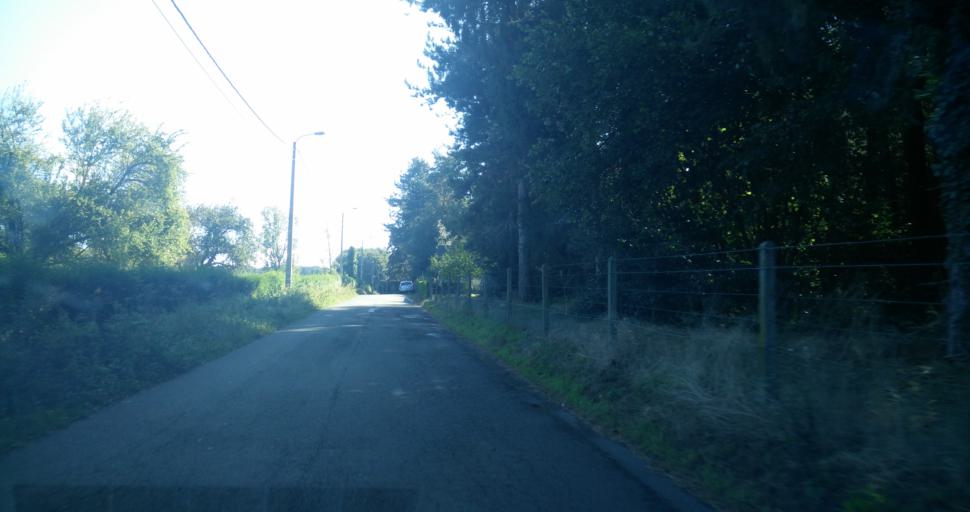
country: BE
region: Flanders
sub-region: Provincie Vlaams-Brabant
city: Halle
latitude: 50.7336
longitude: 4.2642
